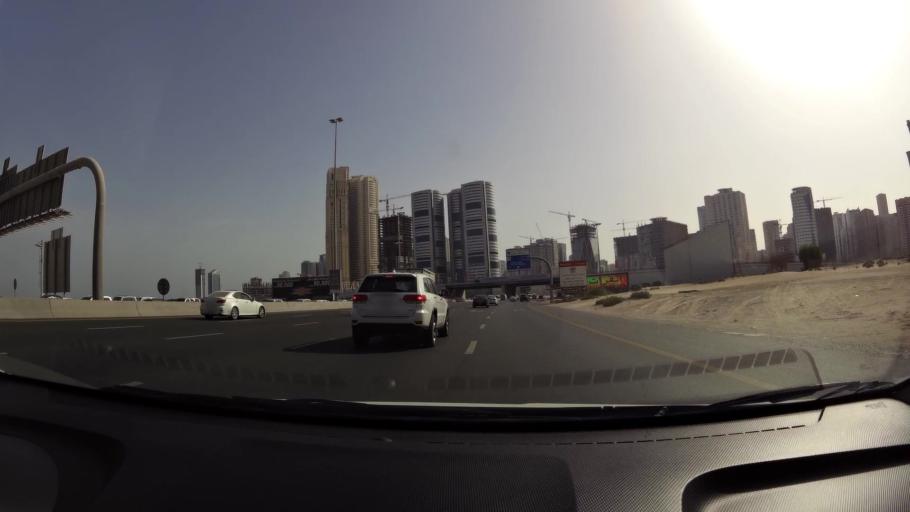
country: AE
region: Ash Shariqah
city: Sharjah
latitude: 25.2984
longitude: 55.3623
